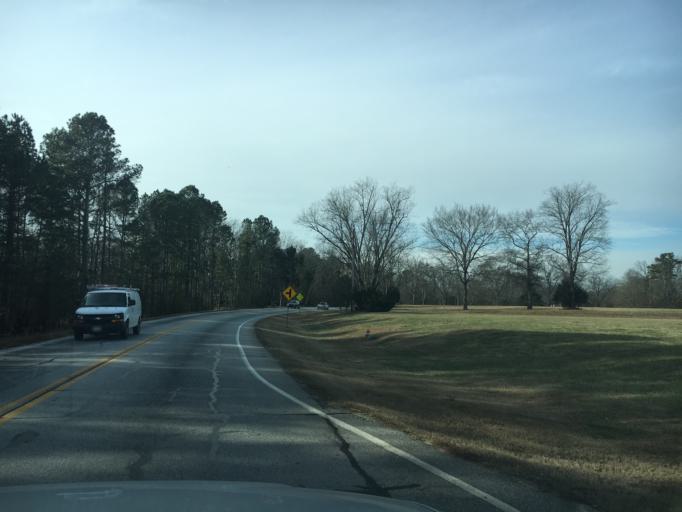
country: US
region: Georgia
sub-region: Jackson County
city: Hoschton
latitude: 34.0885
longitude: -83.7558
